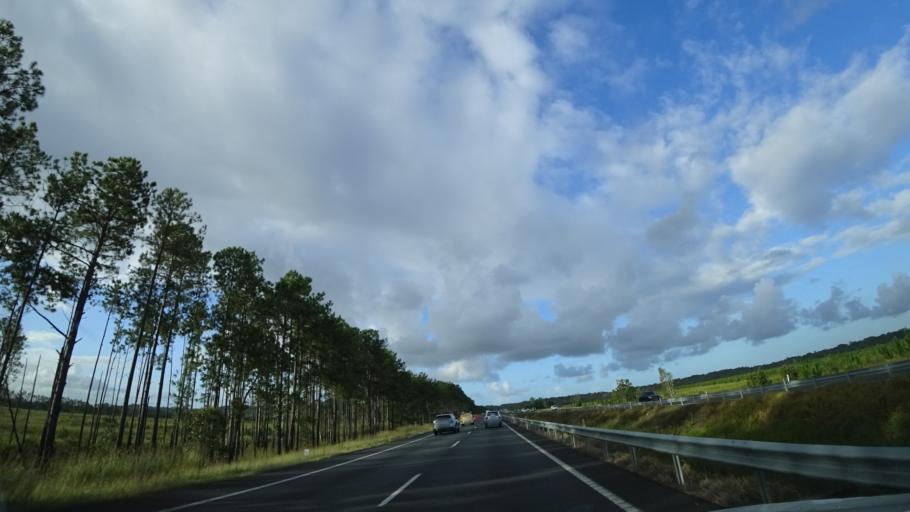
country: AU
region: Queensland
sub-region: Sunshine Coast
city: Little Mountain
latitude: -26.8141
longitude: 153.0378
